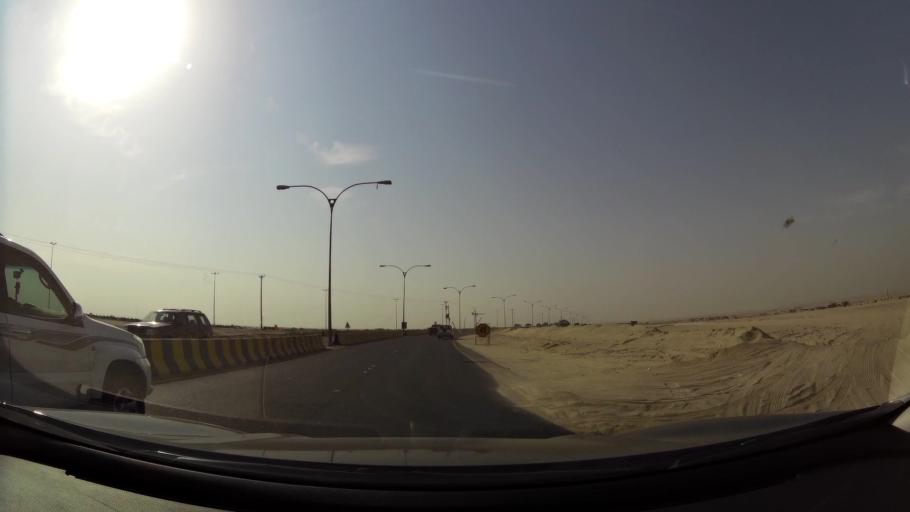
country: KW
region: Al Ahmadi
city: Al Ahmadi
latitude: 28.8919
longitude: 48.0851
